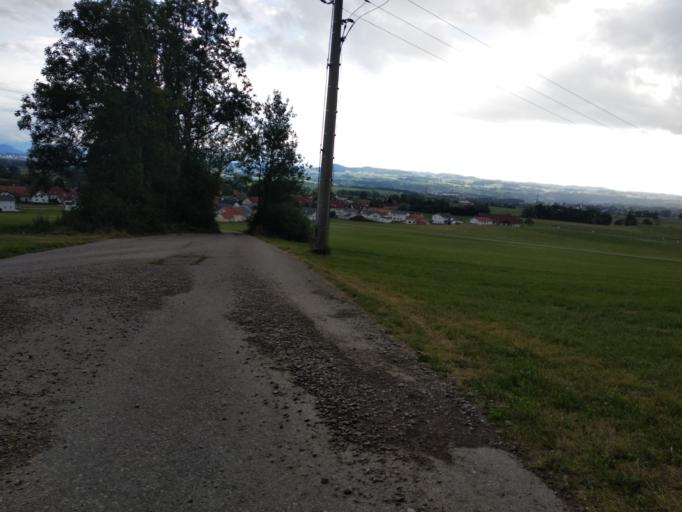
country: DE
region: Bavaria
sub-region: Swabia
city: Haldenwang
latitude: 47.8229
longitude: 10.3336
